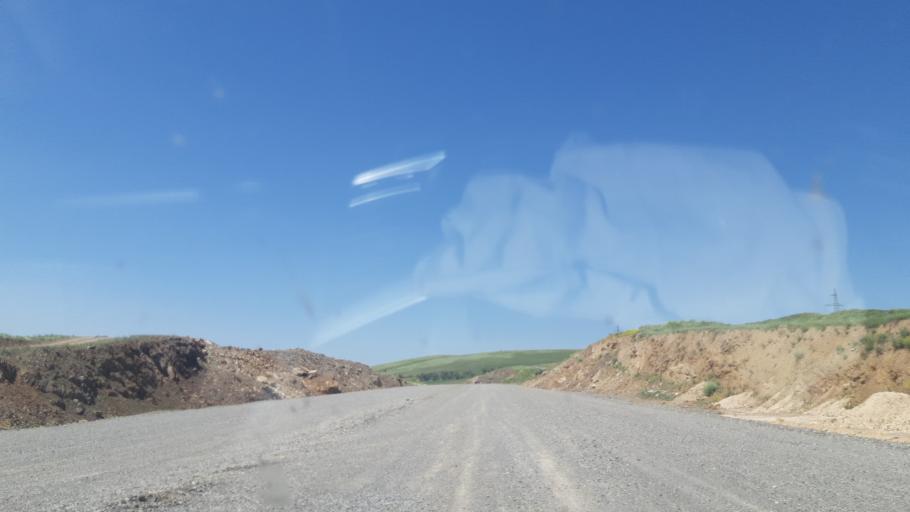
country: KZ
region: Ongtustik Qazaqstan
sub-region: Tulkibas Audany
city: Zhabagly
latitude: 42.5178
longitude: 70.5439
